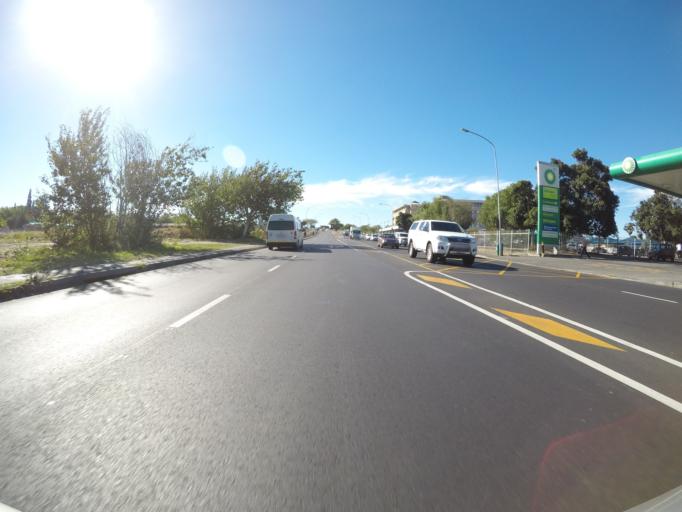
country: ZA
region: Western Cape
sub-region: City of Cape Town
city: Kraaifontein
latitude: -33.9204
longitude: 18.6754
